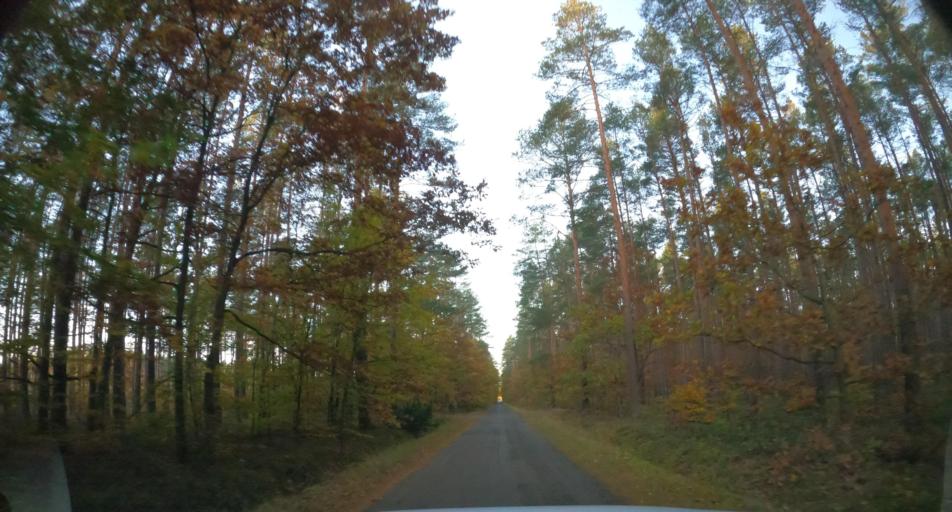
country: PL
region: West Pomeranian Voivodeship
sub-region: Powiat policki
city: Nowe Warpno
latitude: 53.6449
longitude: 14.3264
